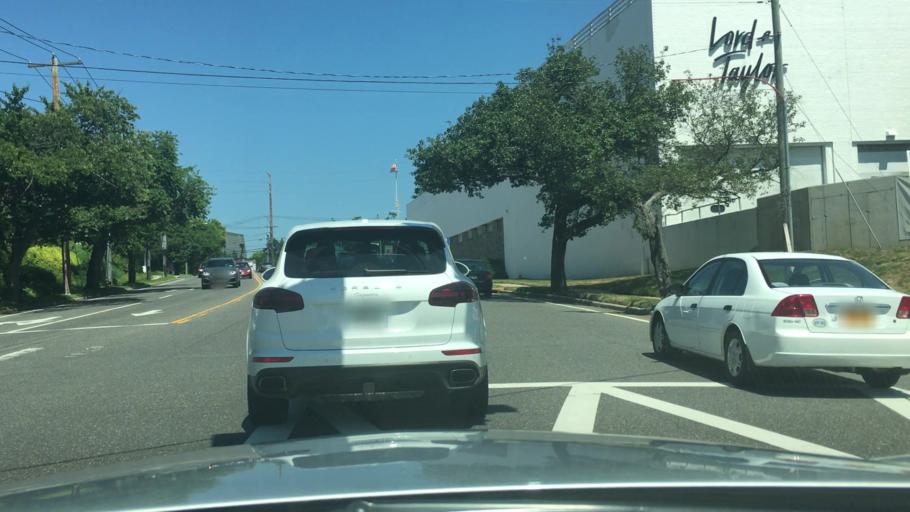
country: US
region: New York
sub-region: Nassau County
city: Manhasset
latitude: 40.7920
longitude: -73.6931
